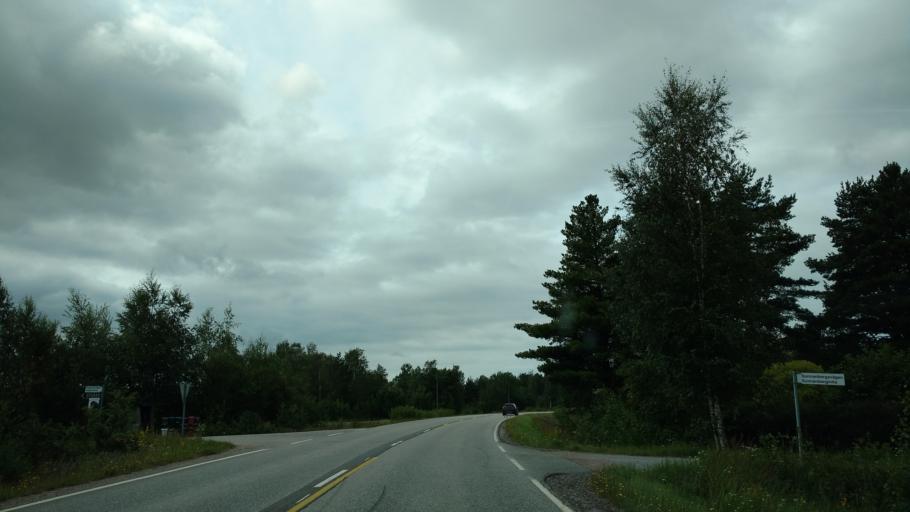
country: FI
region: Varsinais-Suomi
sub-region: Aboland-Turunmaa
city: Dragsfjaerd
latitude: 60.0921
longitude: 22.5316
